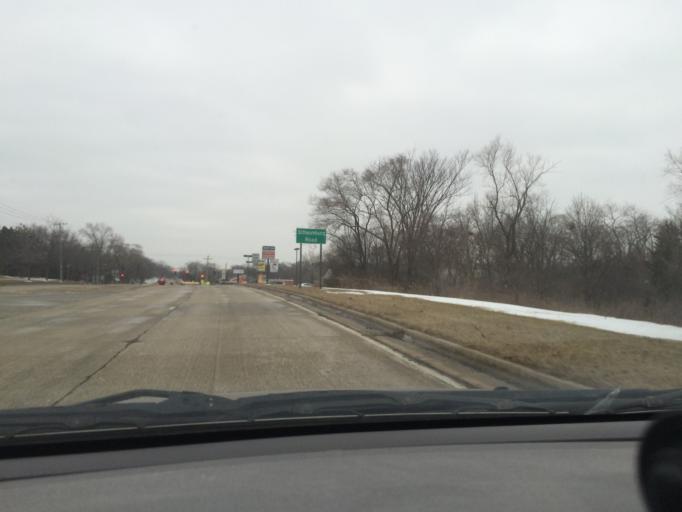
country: US
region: Illinois
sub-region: Cook County
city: Streamwood
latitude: 42.0337
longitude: -88.1797
